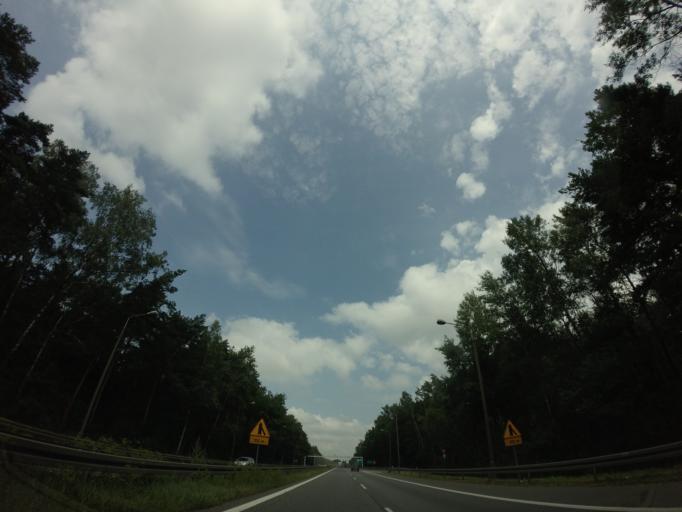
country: PL
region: Silesian Voivodeship
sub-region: Myslowice
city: Myslowice
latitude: 50.1840
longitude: 19.1672
